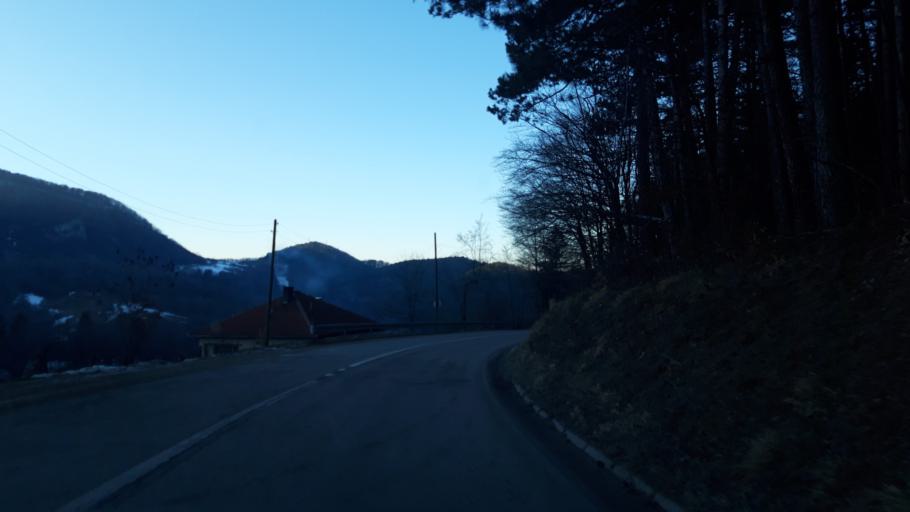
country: BA
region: Republika Srpska
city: Vlasenica
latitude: 44.1677
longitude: 18.9502
